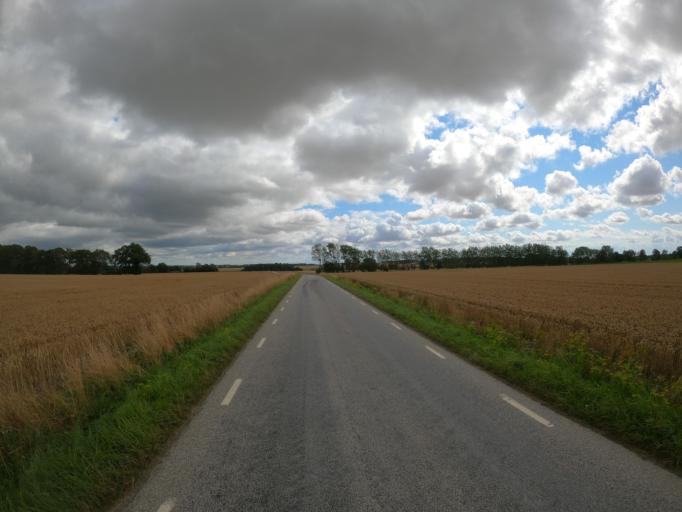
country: SE
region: Skane
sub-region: Lunds Kommun
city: Lund
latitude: 55.7217
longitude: 13.2986
